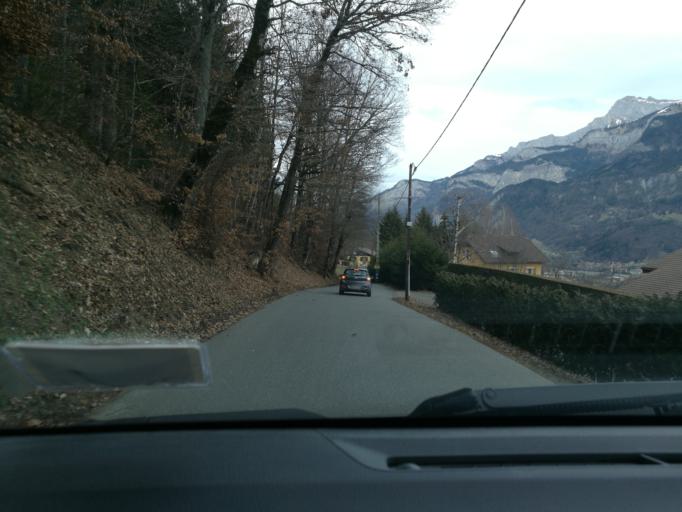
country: FR
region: Rhone-Alpes
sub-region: Departement de la Haute-Savoie
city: Cordon
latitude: 45.9255
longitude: 6.6280
